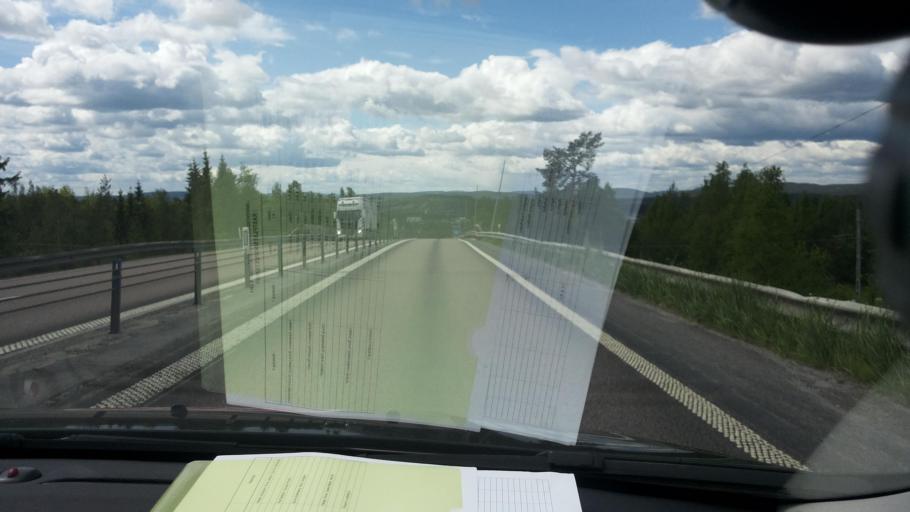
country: SE
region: Vaesternorrland
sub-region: Timra Kommun
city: Soraker
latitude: 62.5309
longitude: 17.4935
